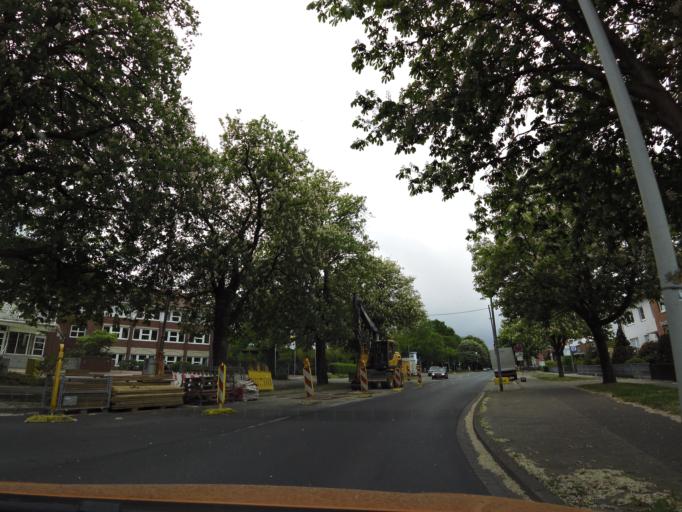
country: DE
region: Lower Saxony
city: Laatzen
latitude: 52.3788
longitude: 9.8073
